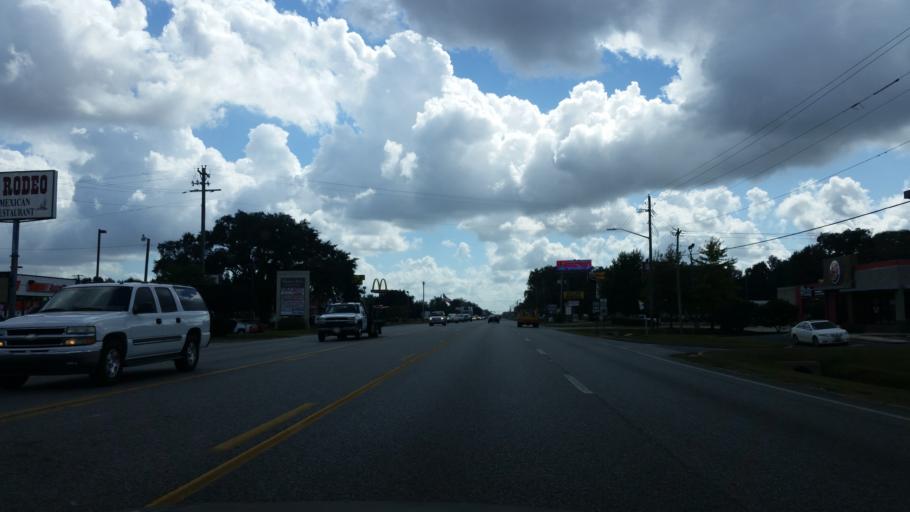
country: US
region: Alabama
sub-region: Baldwin County
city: Robertsdale
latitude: 30.5446
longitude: -87.7084
